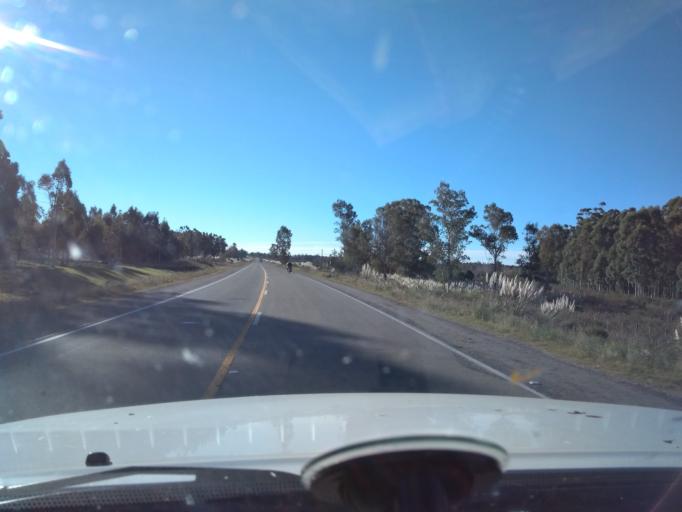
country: UY
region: Canelones
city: Sauce
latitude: -34.6073
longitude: -56.0484
